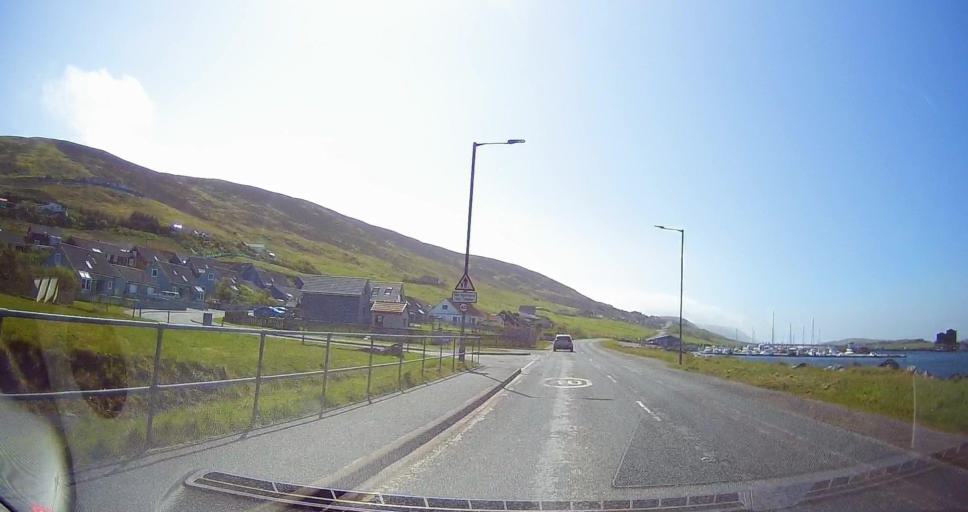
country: GB
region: Scotland
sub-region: Shetland Islands
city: Lerwick
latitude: 60.1394
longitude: -1.2668
